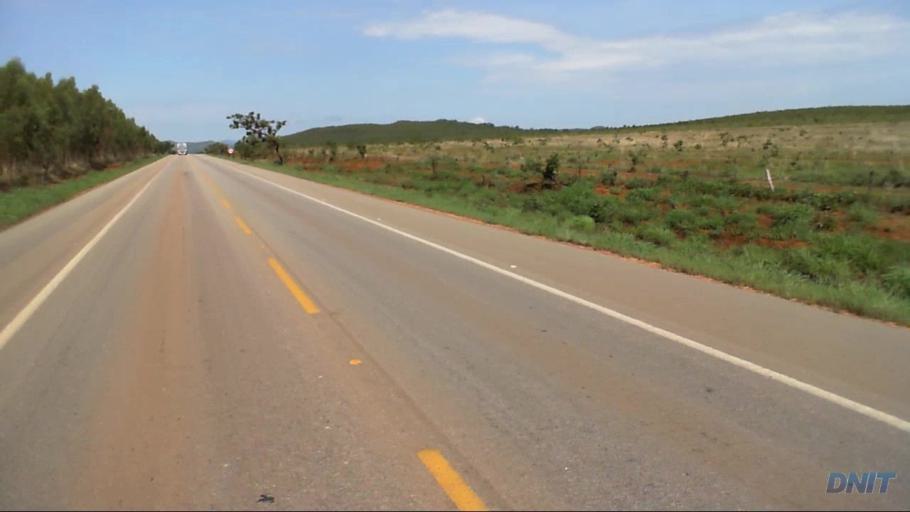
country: BR
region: Goias
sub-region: Barro Alto
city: Barro Alto
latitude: -15.2040
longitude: -48.7387
